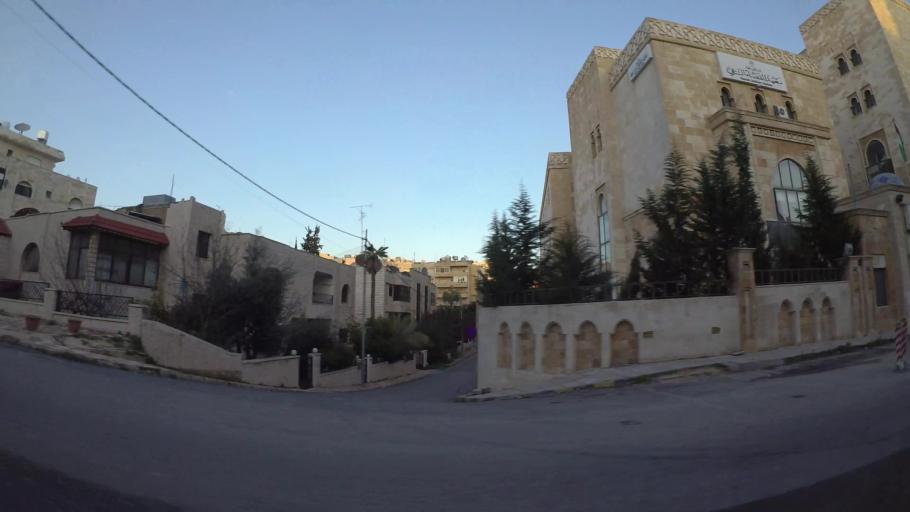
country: JO
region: Amman
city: Al Jubayhah
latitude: 31.9940
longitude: 35.8773
